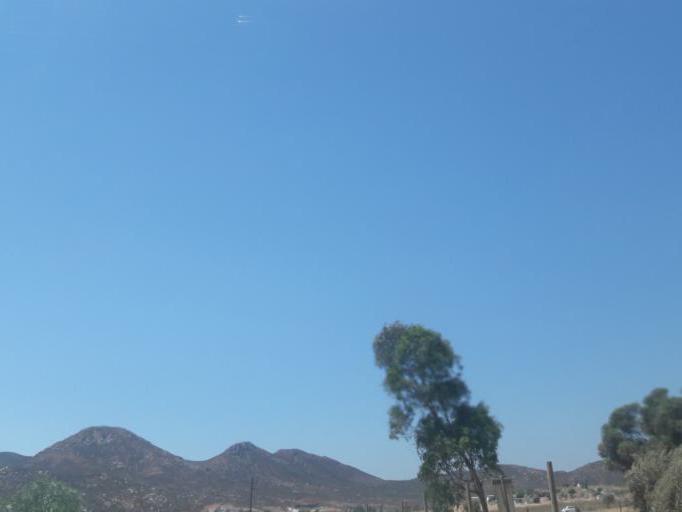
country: MX
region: Baja California
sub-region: Ensenada
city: Rancho Verde
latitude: 32.0911
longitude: -116.6303
